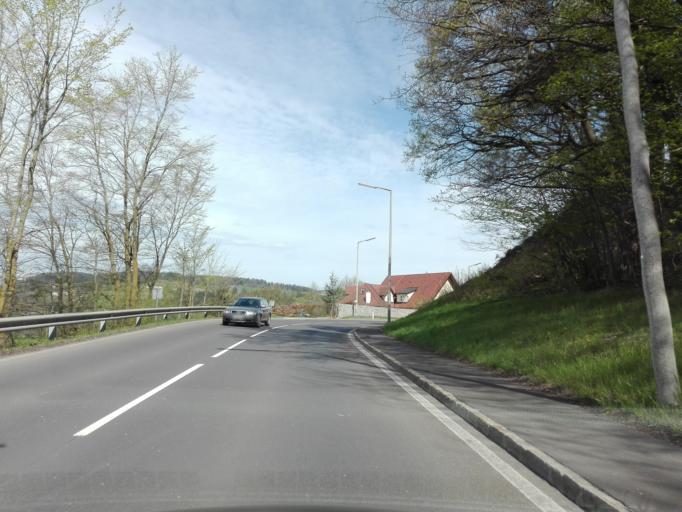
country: AT
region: Upper Austria
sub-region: Linz Stadt
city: Linz
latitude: 48.3237
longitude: 14.2555
